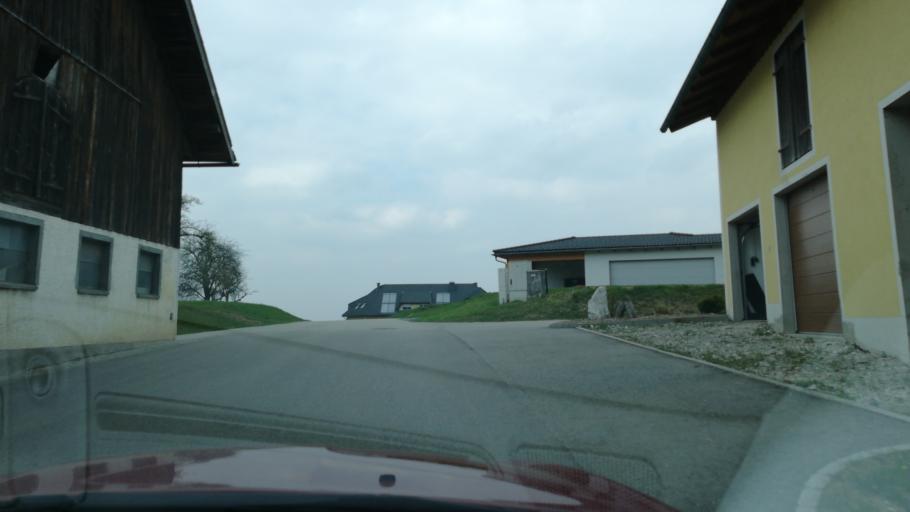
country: AT
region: Upper Austria
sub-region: Politischer Bezirk Vocklabruck
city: Attnang-Puchheim
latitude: 47.9573
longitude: 13.7278
